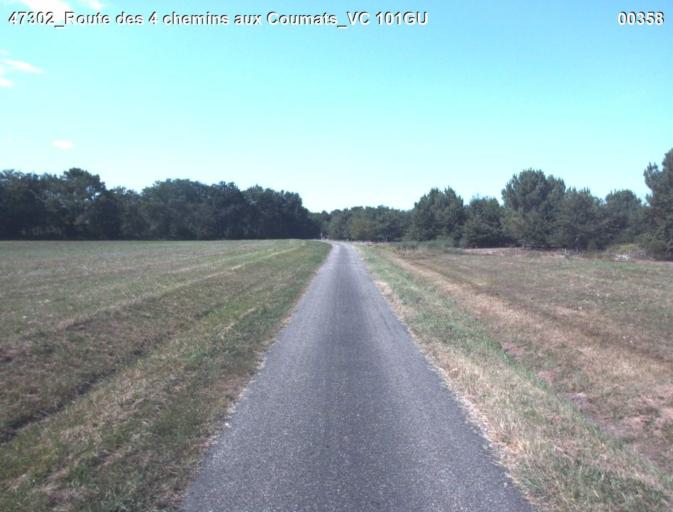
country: FR
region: Aquitaine
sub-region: Departement des Landes
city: Gabarret
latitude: 44.0191
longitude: 0.0864
